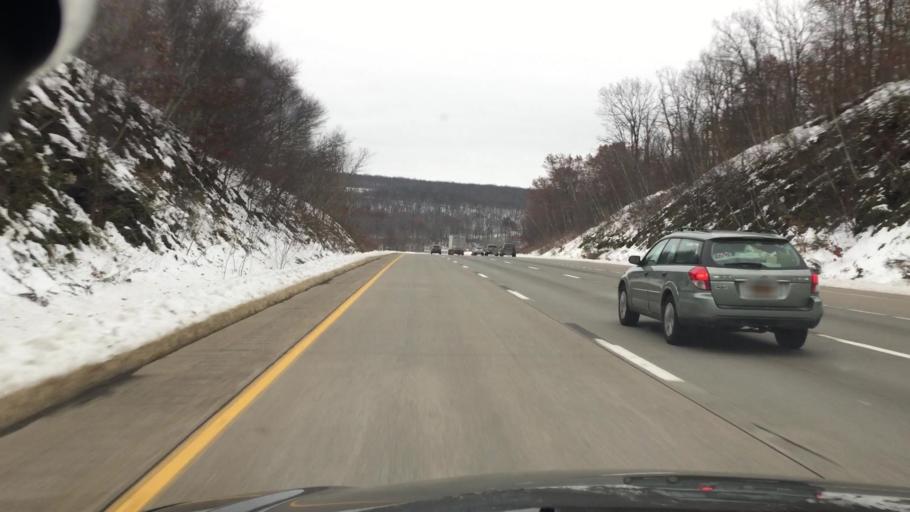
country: US
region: Pennsylvania
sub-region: Luzerne County
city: Freeland
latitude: 41.0876
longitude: -75.9632
